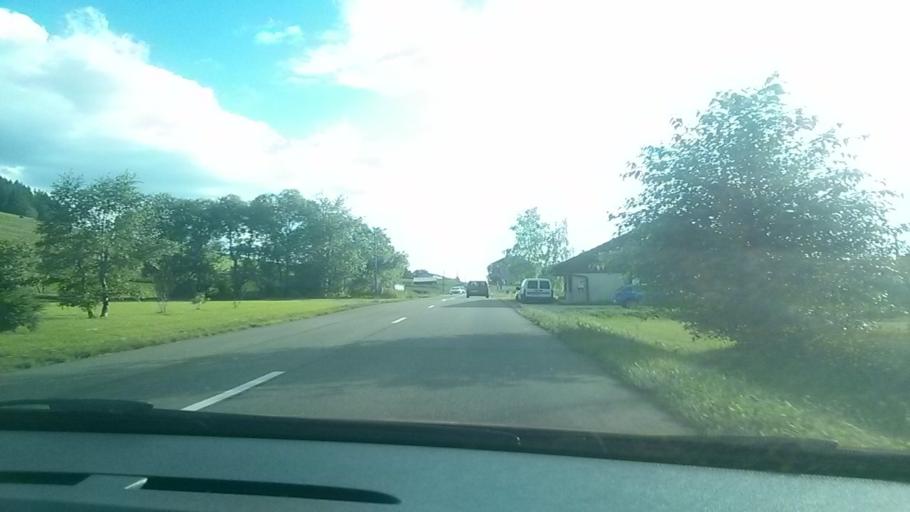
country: FR
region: Franche-Comte
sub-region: Departement du Jura
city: Les Rousses
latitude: 46.5138
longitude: 6.1145
